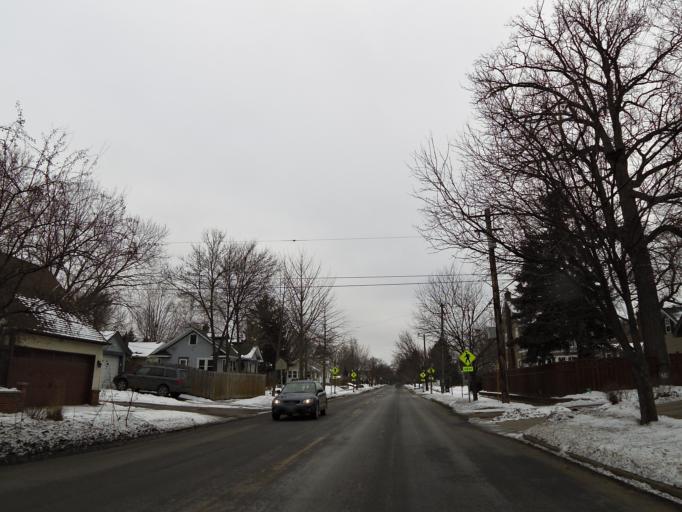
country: US
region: Minnesota
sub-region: Ramsey County
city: Falcon Heights
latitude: 44.9314
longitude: -93.1925
